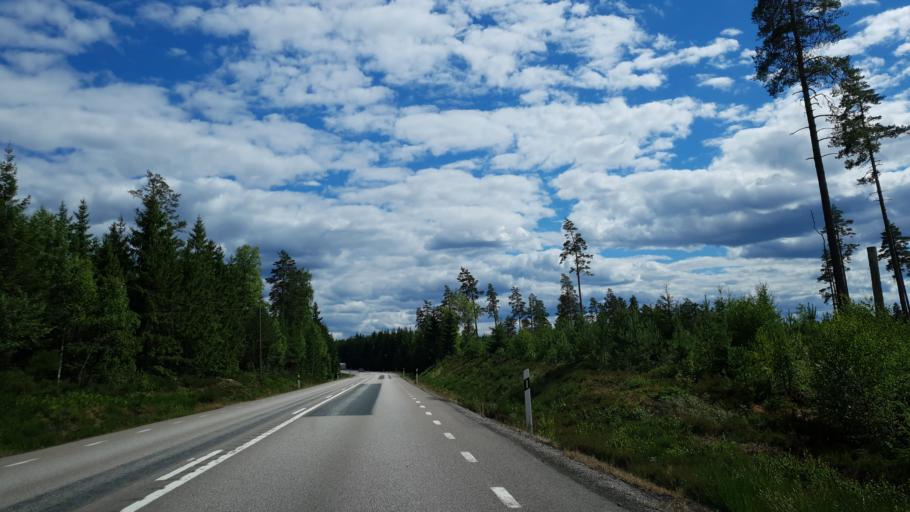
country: SE
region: Kronoberg
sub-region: Uppvidinge Kommun
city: Lenhovda
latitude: 56.8824
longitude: 15.3774
